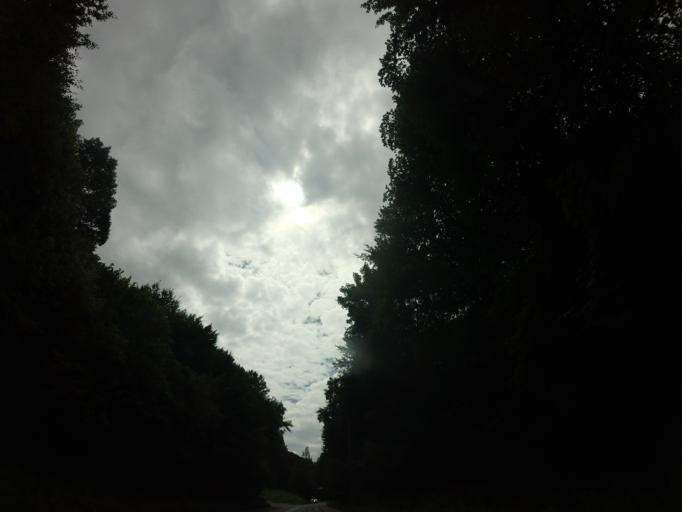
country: PL
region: Lublin Voivodeship
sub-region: Powiat pulawski
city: Kazimierz Dolny
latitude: 51.3147
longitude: 21.9528
